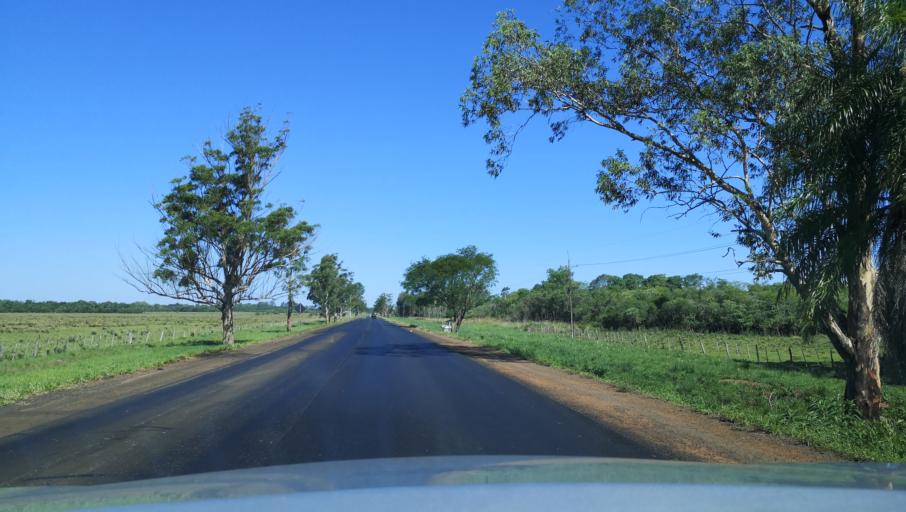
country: PY
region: Itapua
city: General Delgado
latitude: -27.1107
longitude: -56.4214
